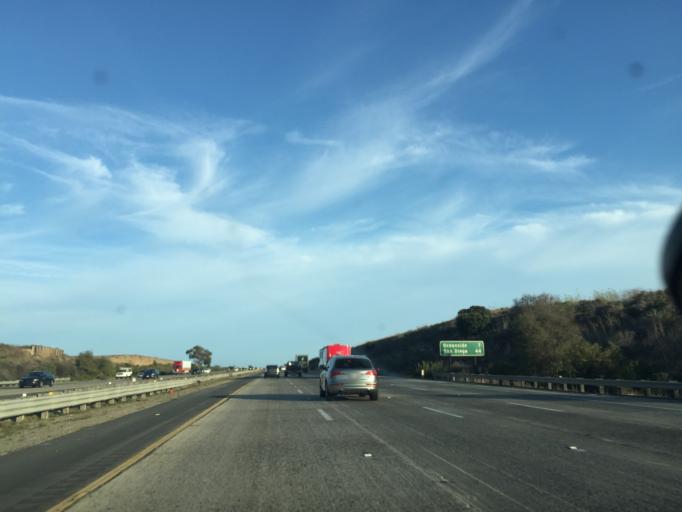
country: US
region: California
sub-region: San Diego County
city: Camp Pendleton South
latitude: 33.2912
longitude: -117.4568
